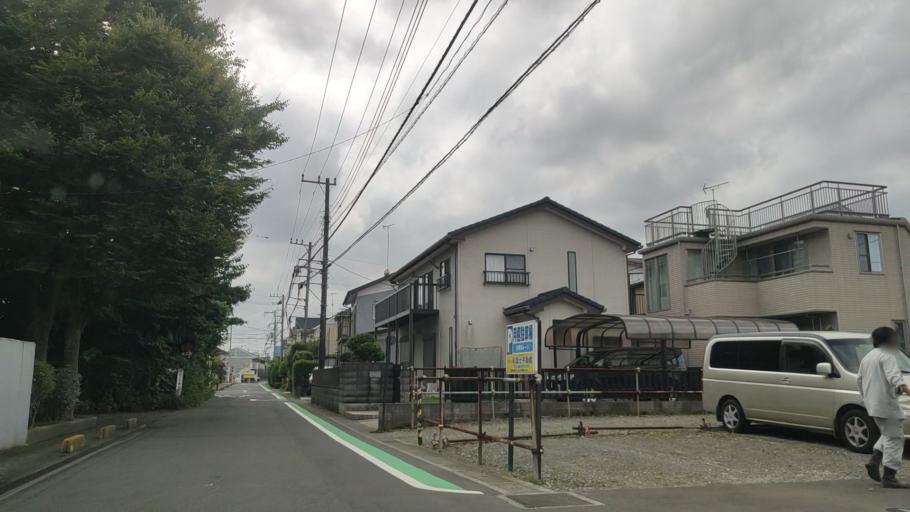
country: JP
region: Kanagawa
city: Minami-rinkan
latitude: 35.5042
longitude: 139.4396
